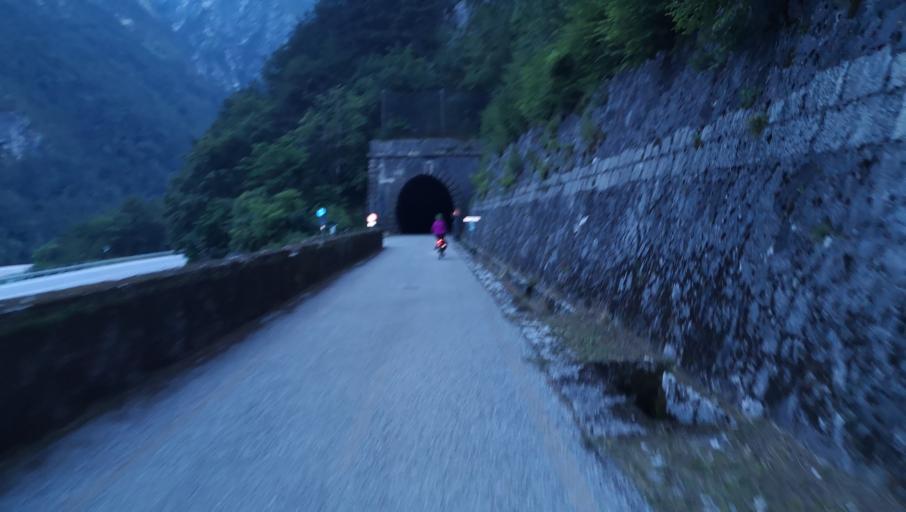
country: IT
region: Friuli Venezia Giulia
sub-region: Provincia di Udine
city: Chiusaforte
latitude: 46.3995
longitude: 13.2837
